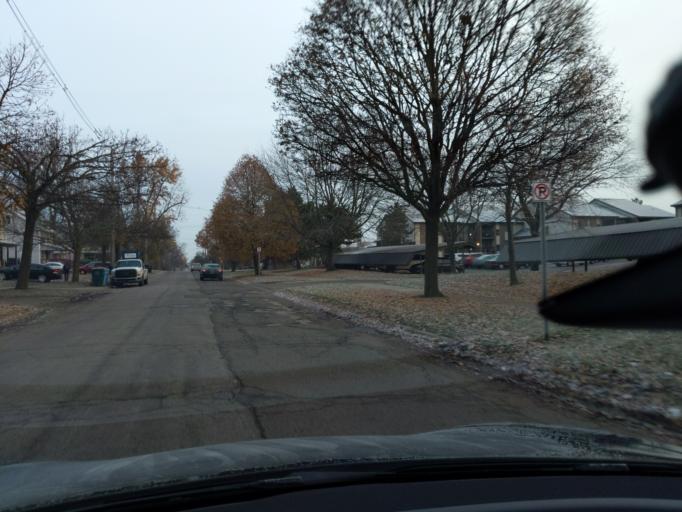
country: US
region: Michigan
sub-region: Ingham County
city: Lansing
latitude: 42.7276
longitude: -84.5647
